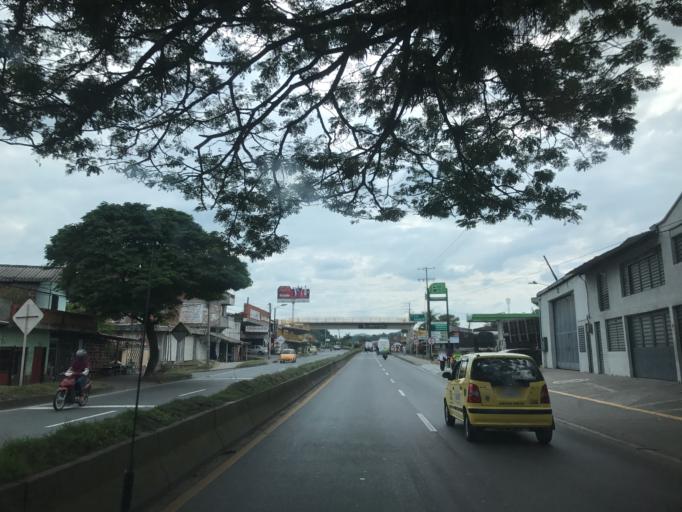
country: CO
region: Valle del Cauca
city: Cartago
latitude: 4.7553
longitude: -75.8988
